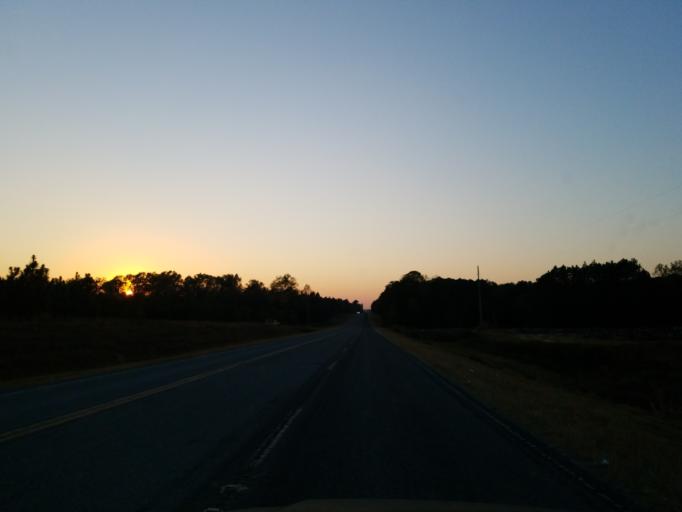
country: US
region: Georgia
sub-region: Ben Hill County
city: Fitzgerald
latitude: 31.7204
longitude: -83.4168
